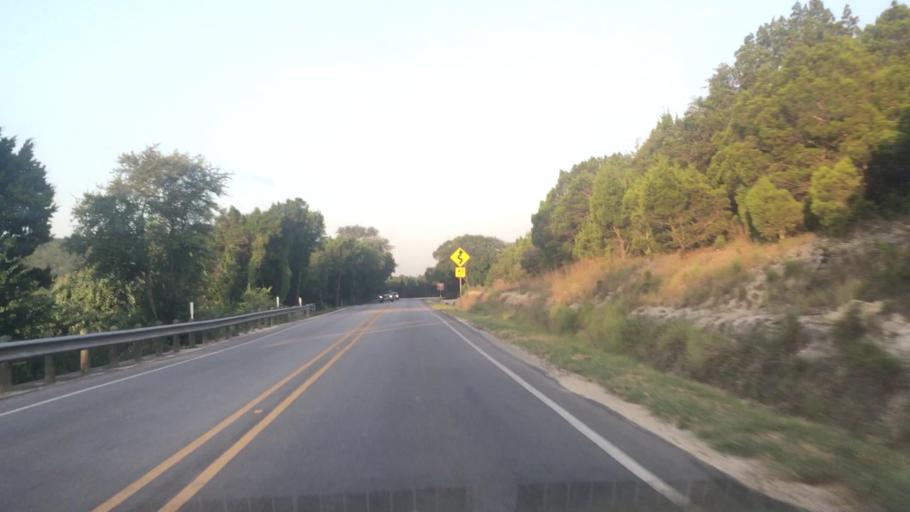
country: US
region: Texas
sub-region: Williamson County
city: Anderson Mill
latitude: 30.4439
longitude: -97.8635
